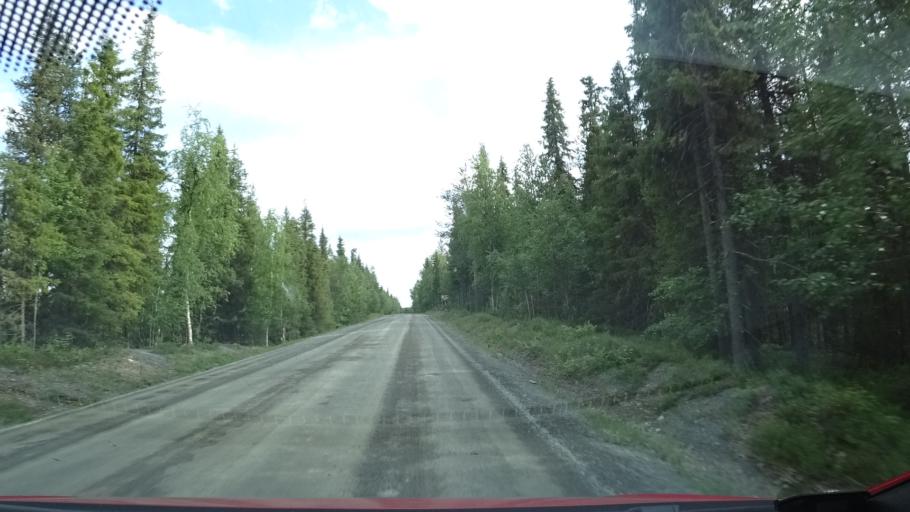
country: FI
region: Lapland
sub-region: Tunturi-Lappi
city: Kittilae
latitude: 67.9105
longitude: 25.0772
